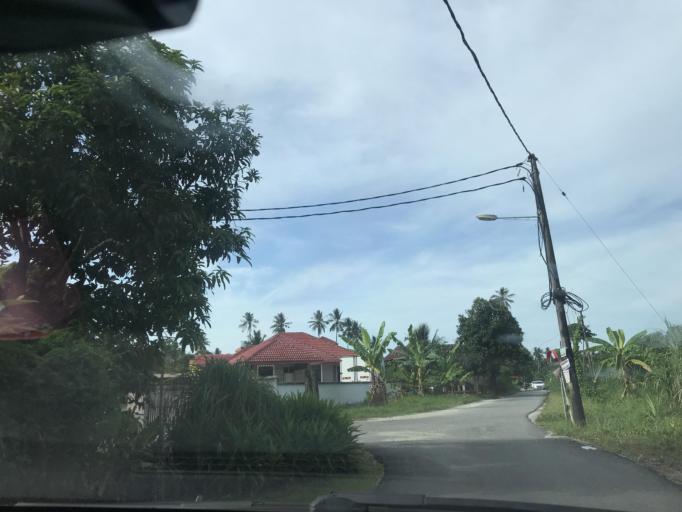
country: MY
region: Kelantan
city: Kota Bharu
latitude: 6.1370
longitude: 102.2222
